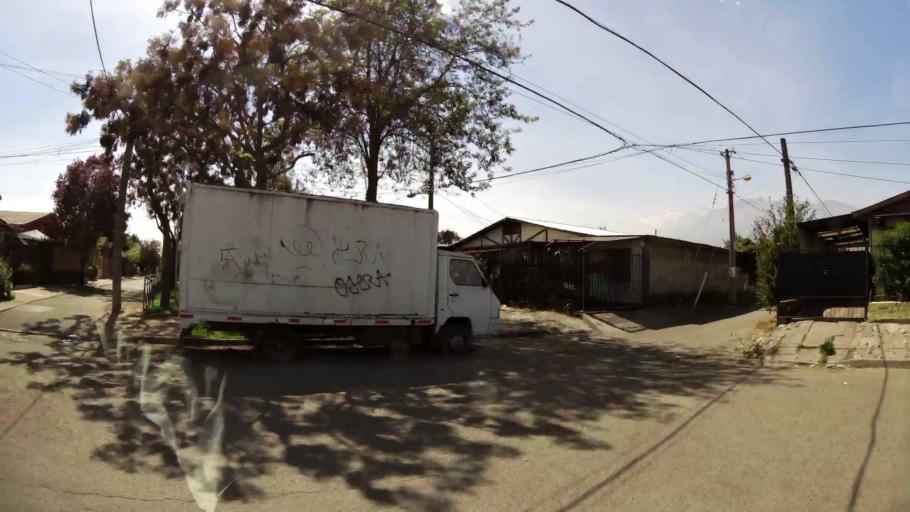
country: CL
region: Santiago Metropolitan
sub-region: Provincia de Cordillera
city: Puente Alto
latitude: -33.5725
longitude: -70.5771
